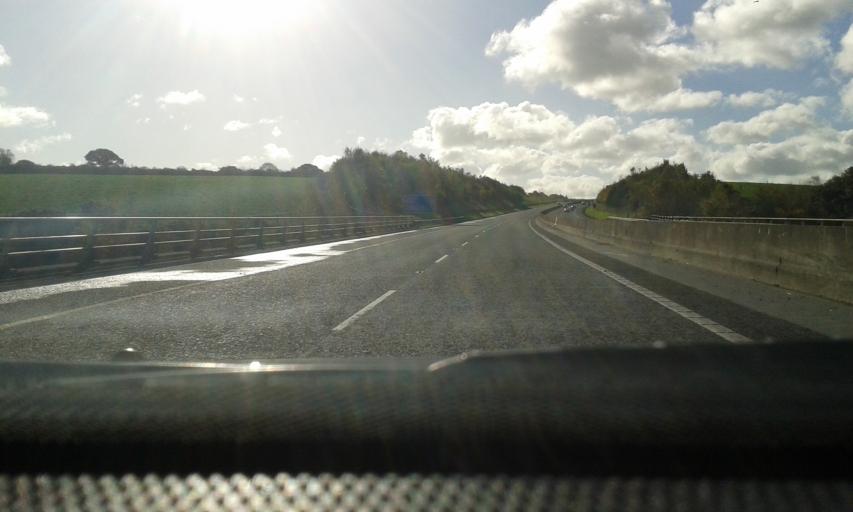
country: IE
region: Munster
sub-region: County Cork
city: Rathcormac
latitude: 52.0493
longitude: -8.3082
